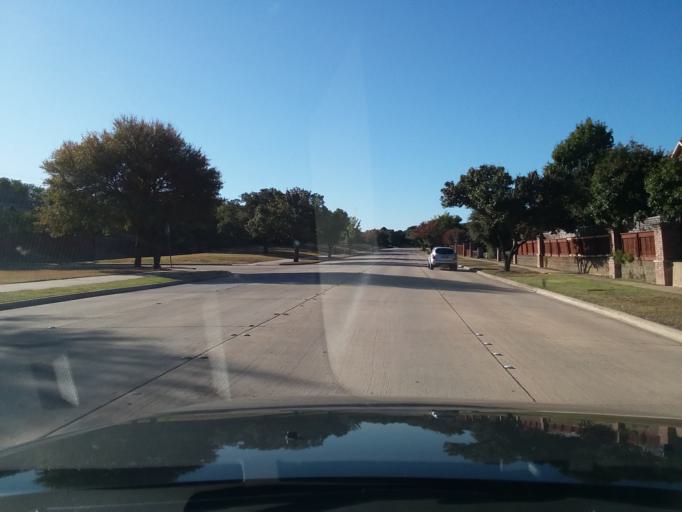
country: US
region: Texas
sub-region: Denton County
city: Lewisville
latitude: 33.0171
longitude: -97.0274
